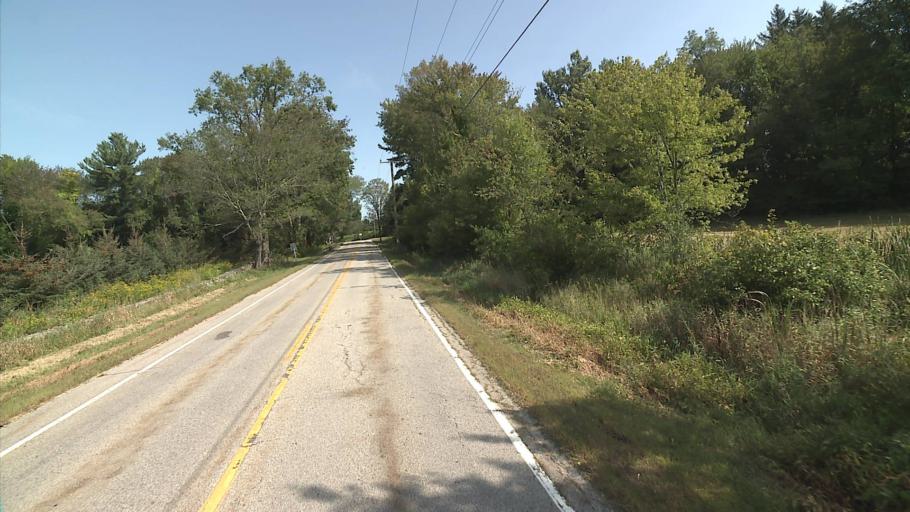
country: US
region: Connecticut
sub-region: Windham County
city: South Woodstock
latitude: 41.9115
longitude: -71.9567
